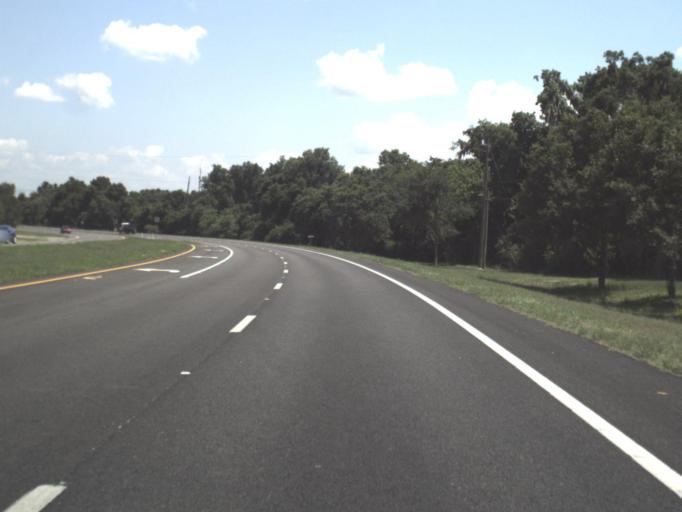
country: US
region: Florida
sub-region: Alachua County
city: Gainesville
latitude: 29.6154
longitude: -82.2556
